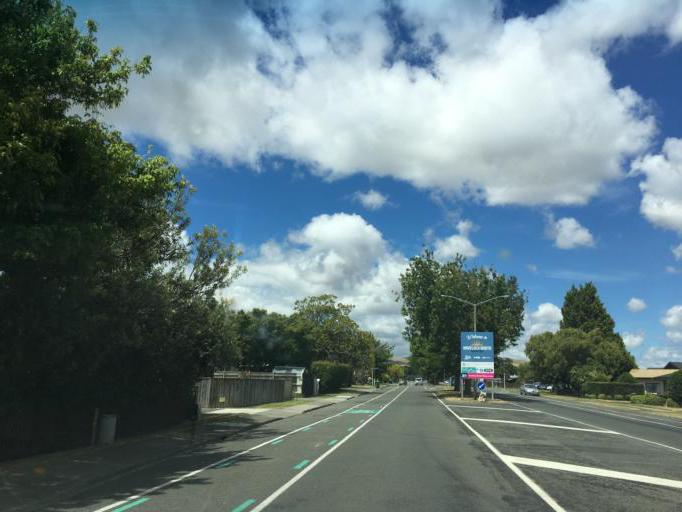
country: NZ
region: Hawke's Bay
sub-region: Hastings District
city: Hastings
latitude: -39.6613
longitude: 176.8843
